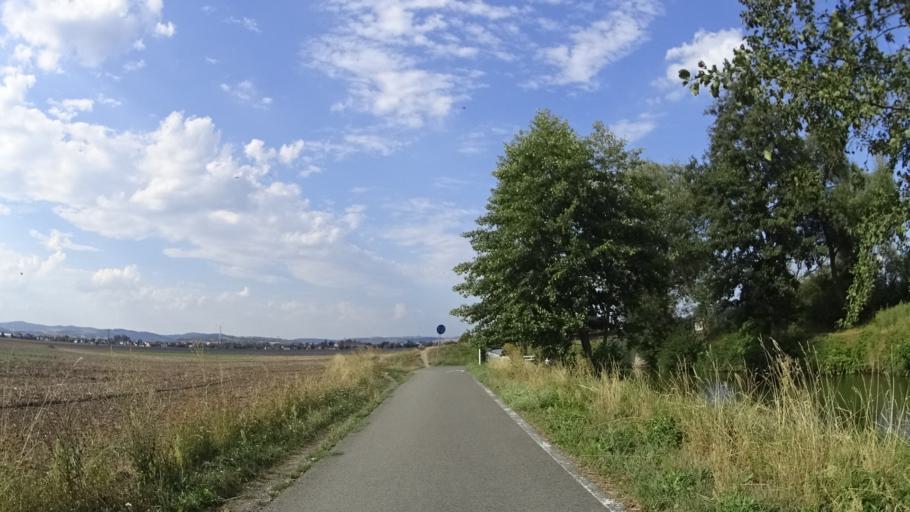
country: CZ
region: Zlin
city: Babice
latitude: 49.1071
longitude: 17.4781
